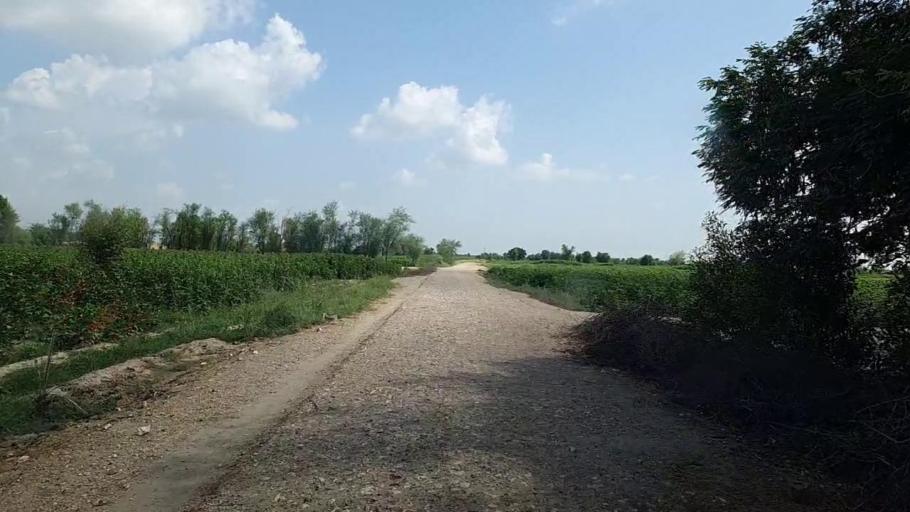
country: PK
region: Sindh
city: Kandiaro
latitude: 26.9892
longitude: 68.3053
